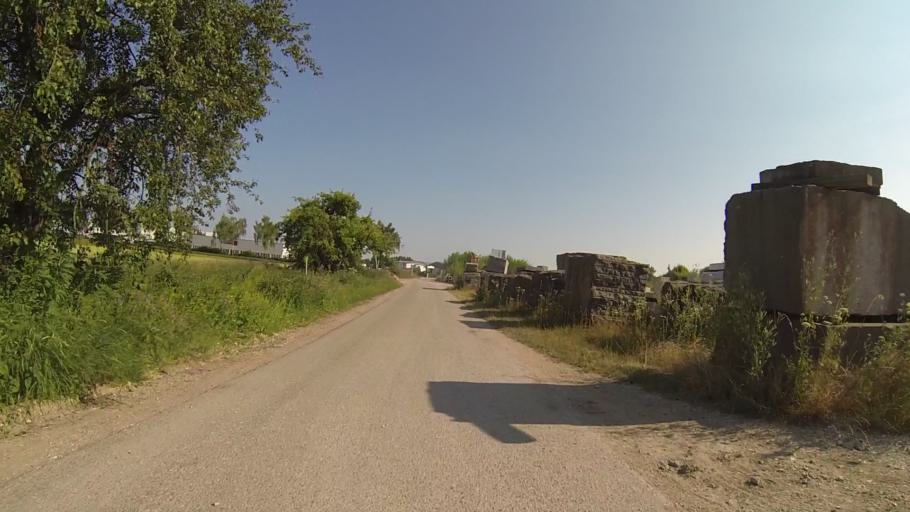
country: DE
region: Baden-Wuerttemberg
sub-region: Tuebingen Region
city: Erbach
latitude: 48.3318
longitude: 9.9027
